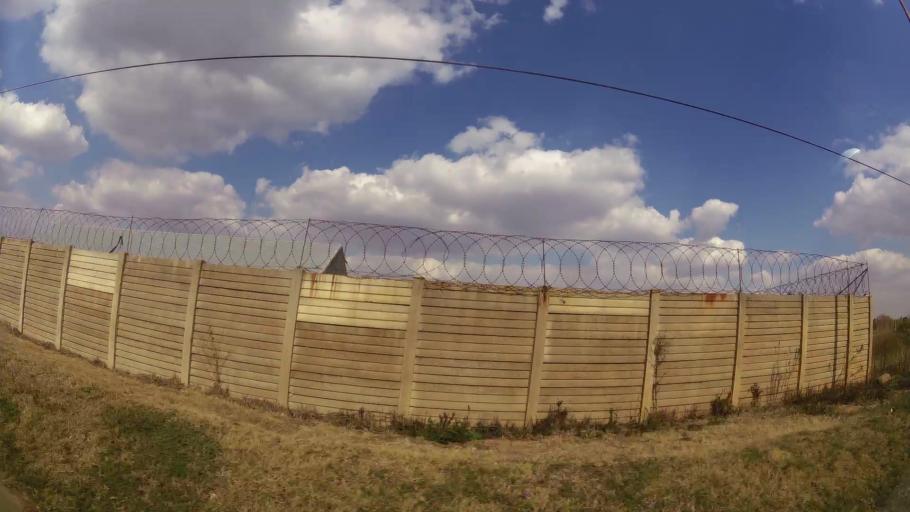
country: ZA
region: Mpumalanga
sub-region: Nkangala District Municipality
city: Delmas
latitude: -26.1348
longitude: 28.6801
